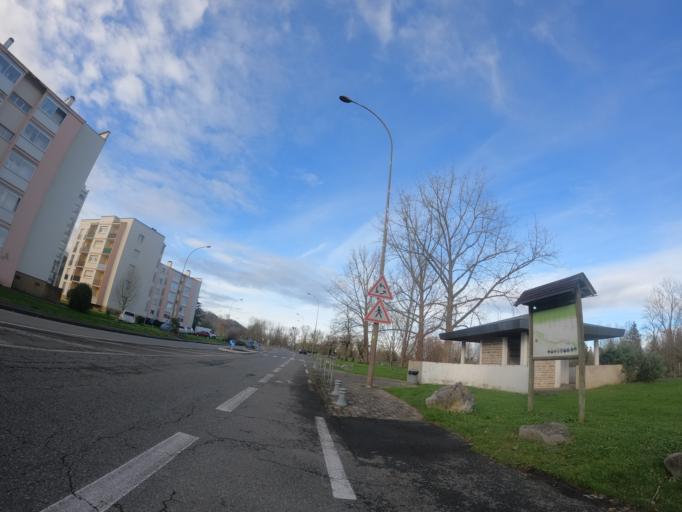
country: FR
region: Aquitaine
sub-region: Departement des Pyrenees-Atlantiques
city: Billere
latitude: 43.2924
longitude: -0.3952
